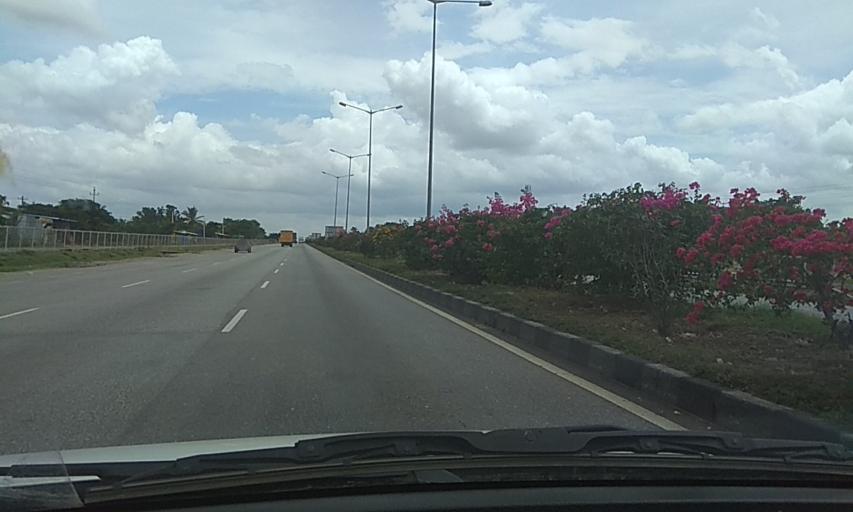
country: IN
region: Karnataka
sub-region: Tumkur
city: Sira
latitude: 13.6081
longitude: 76.9571
